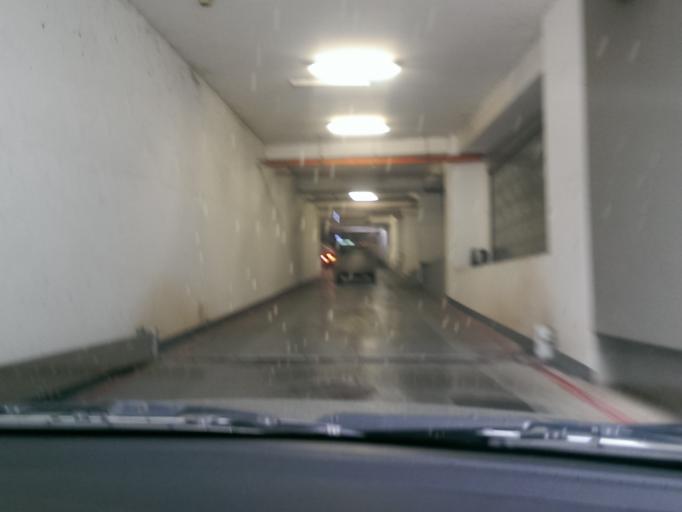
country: TW
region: Taiwan
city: Fengyuan
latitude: 24.2526
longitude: 120.5992
